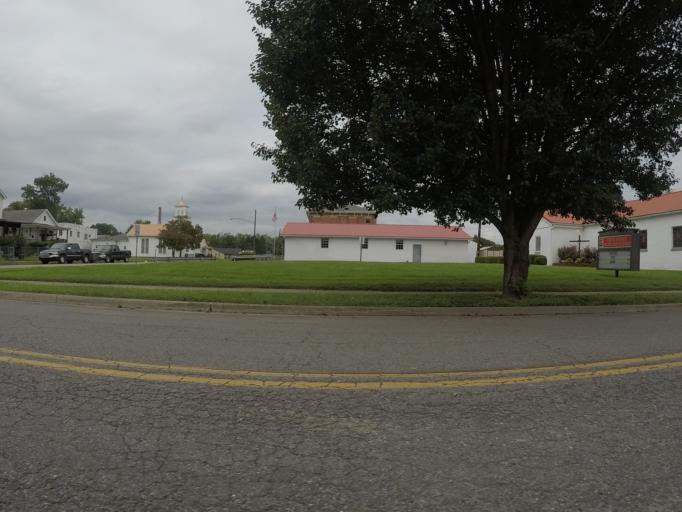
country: US
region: West Virginia
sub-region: Cabell County
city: Huntington
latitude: 38.4277
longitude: -82.3875
